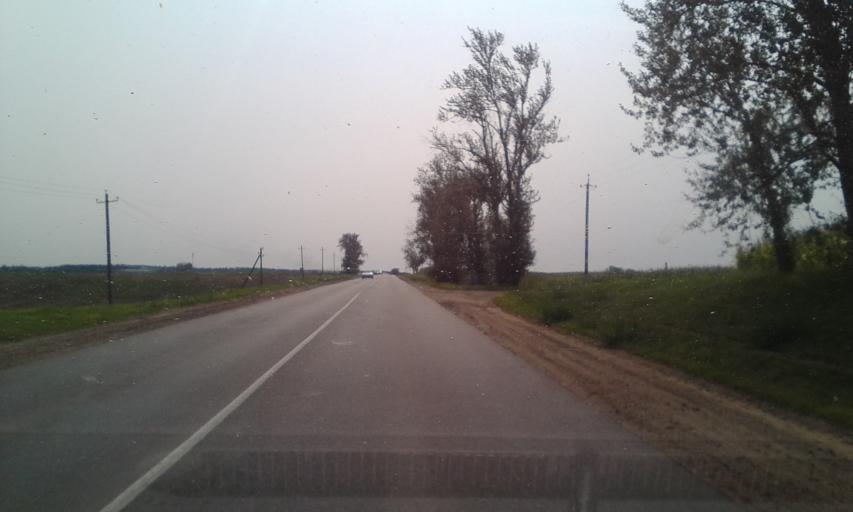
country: BY
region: Minsk
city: Hatava
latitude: 53.7917
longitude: 27.6499
